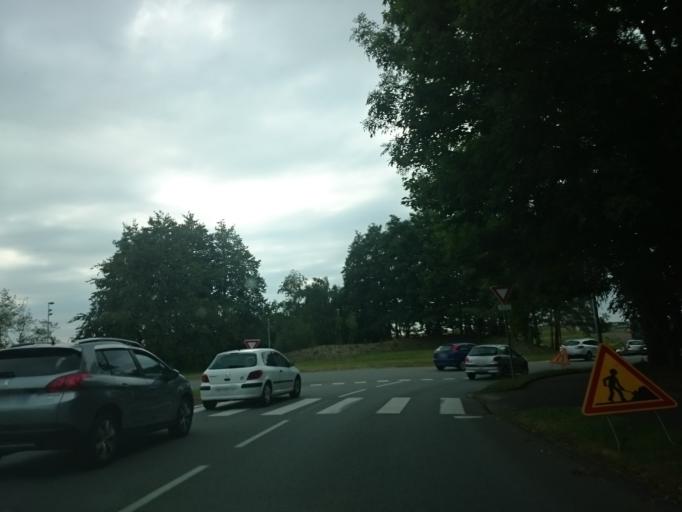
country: FR
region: Brittany
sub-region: Departement du Finistere
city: Bohars
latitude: 48.4130
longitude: -4.5071
